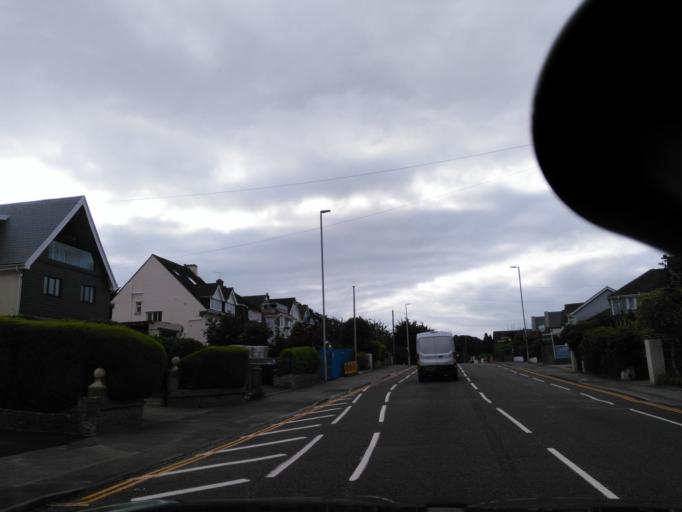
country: GB
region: England
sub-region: Dorset
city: Parkstone
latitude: 50.7111
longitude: -1.9482
